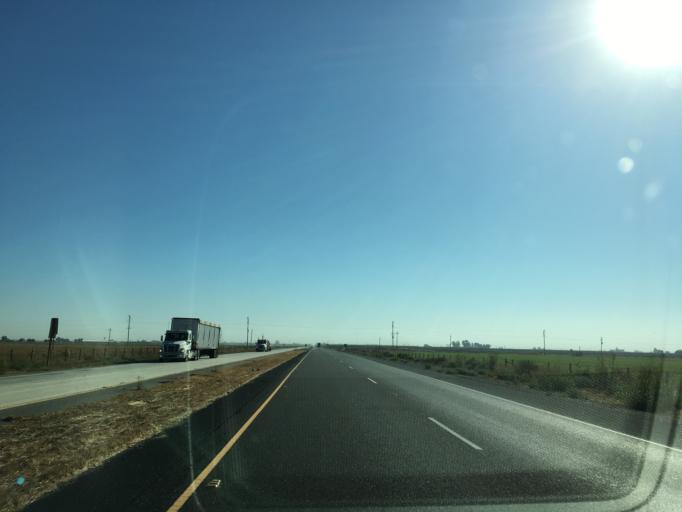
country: US
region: California
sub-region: Madera County
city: Chowchilla
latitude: 37.0833
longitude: -120.3514
